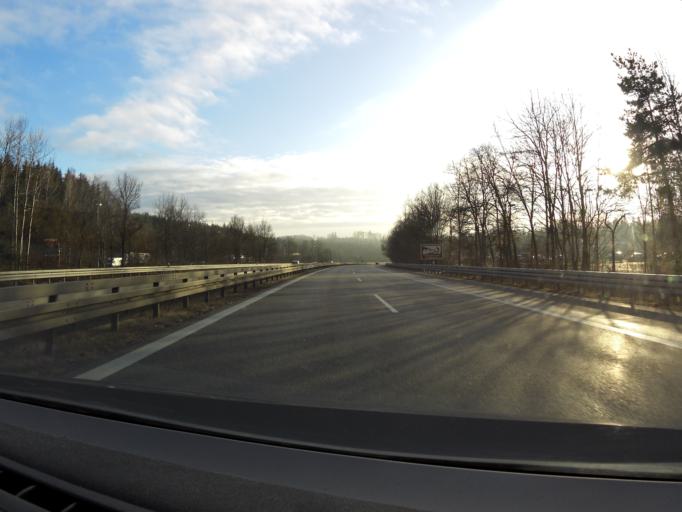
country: DE
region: Bavaria
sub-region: Upper Bavaria
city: Wolfratshausen
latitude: 47.9288
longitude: 11.4027
